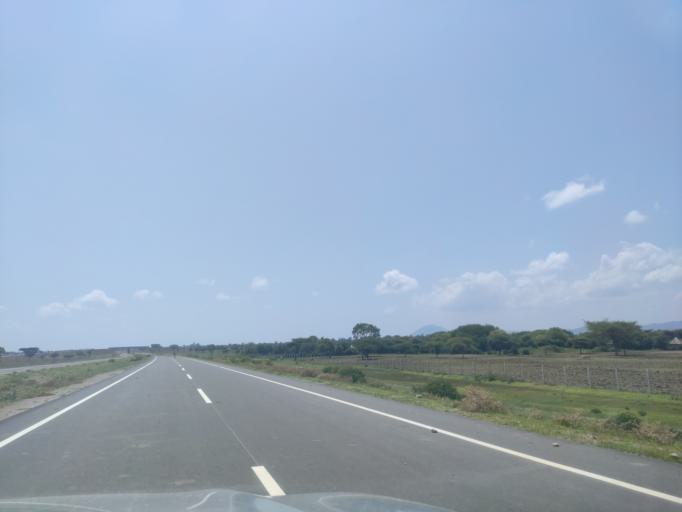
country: ET
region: Oromiya
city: Ziway
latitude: 8.2280
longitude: 38.8705
